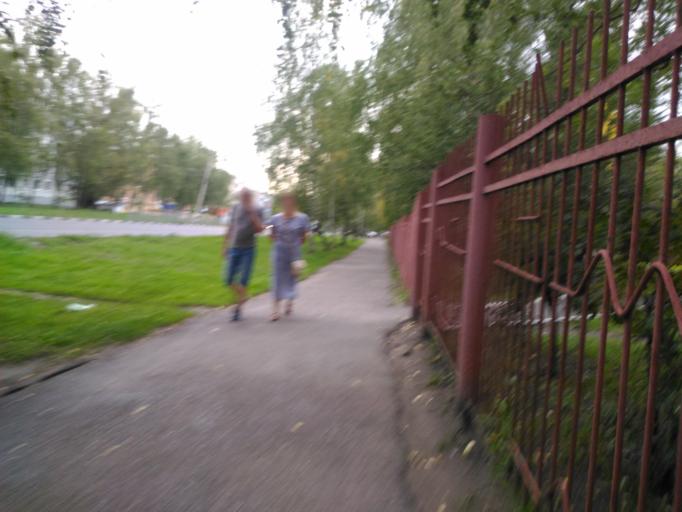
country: RU
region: Ulyanovsk
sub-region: Ulyanovskiy Rayon
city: Ulyanovsk
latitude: 54.2644
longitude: 48.3348
